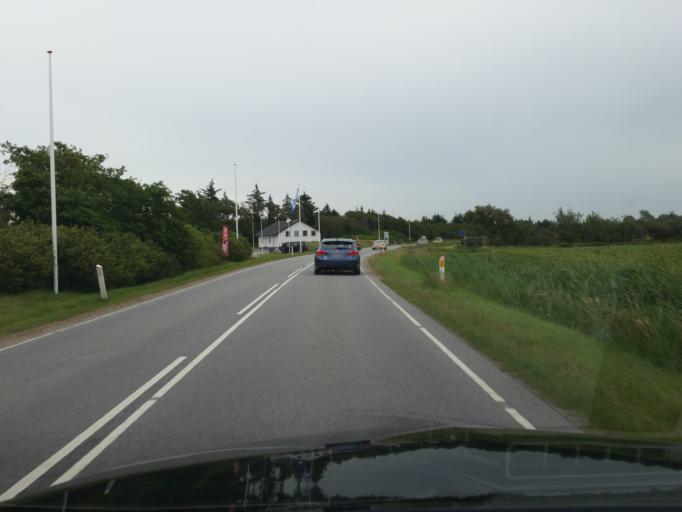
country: DK
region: South Denmark
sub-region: Varde Kommune
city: Oksbol
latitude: 55.8036
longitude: 8.2265
